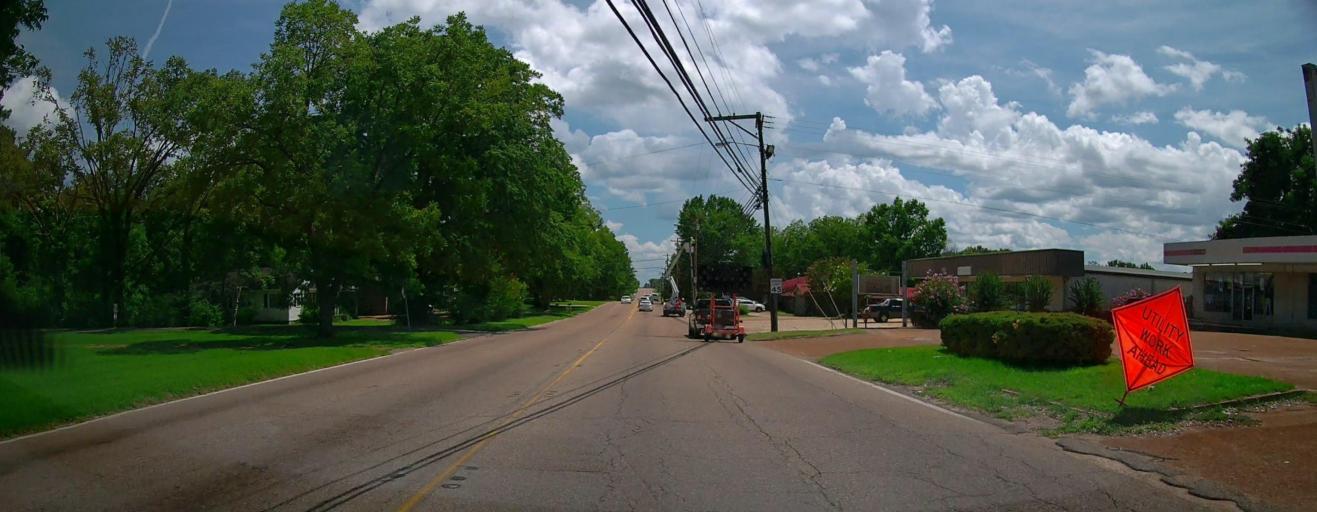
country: US
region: Mississippi
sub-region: Lee County
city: Verona
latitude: 34.1917
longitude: -88.7200
